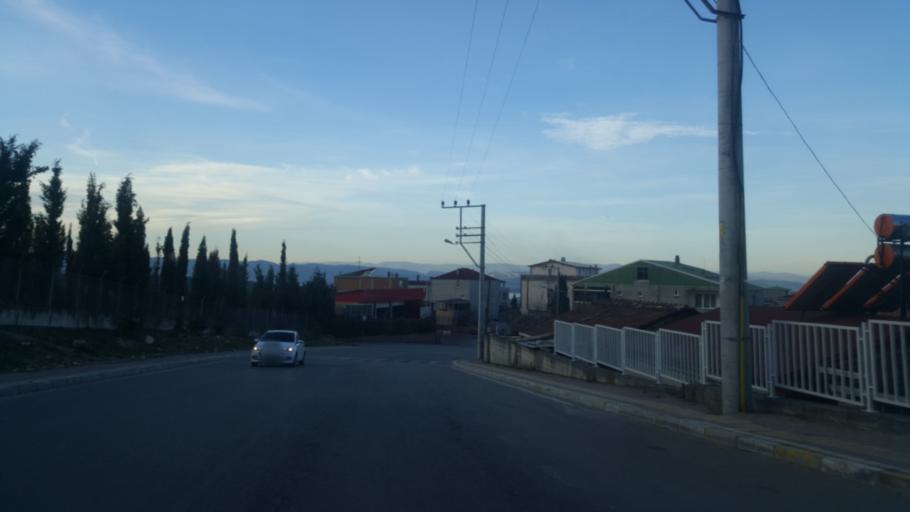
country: TR
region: Kocaeli
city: Tavsancil
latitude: 40.7934
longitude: 29.5512
